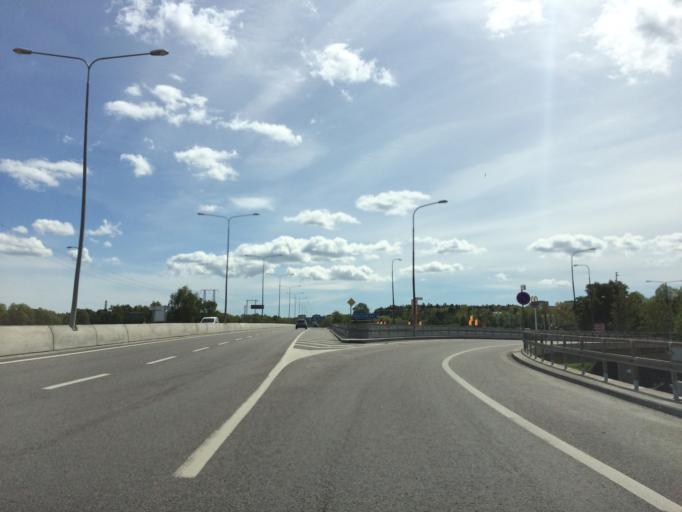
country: SE
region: Stockholm
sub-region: Stockholms Kommun
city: Arsta
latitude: 59.2749
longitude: 18.0108
